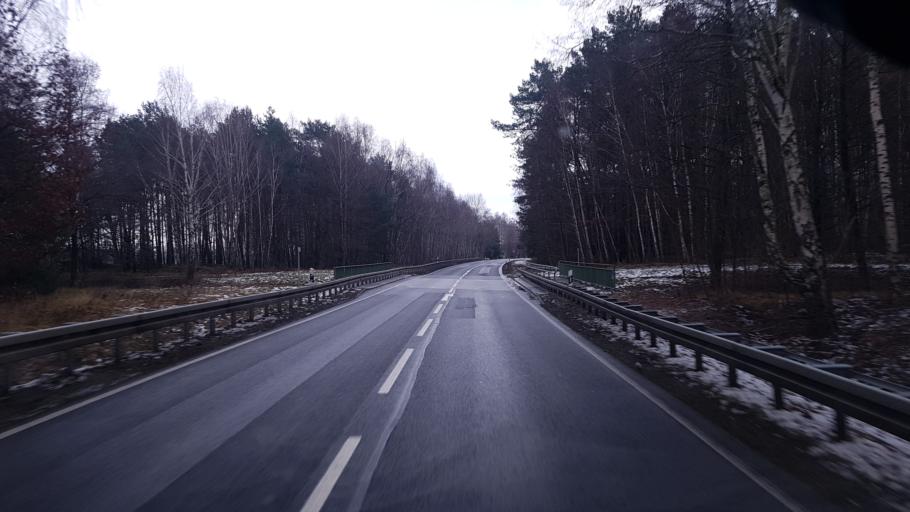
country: DE
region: Brandenburg
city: Janschwalde
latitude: 51.8411
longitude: 14.4678
